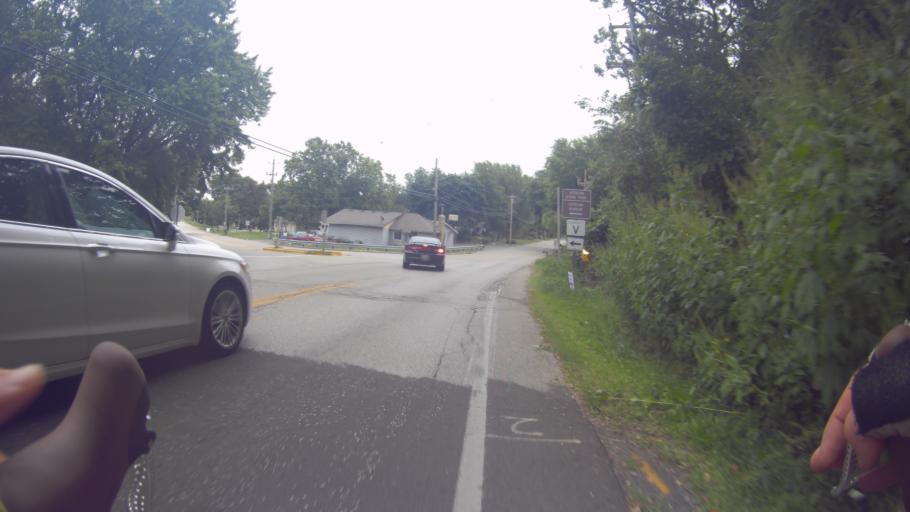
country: US
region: Wisconsin
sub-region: Jefferson County
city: Lake Mills
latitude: 43.0925
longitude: -88.9192
